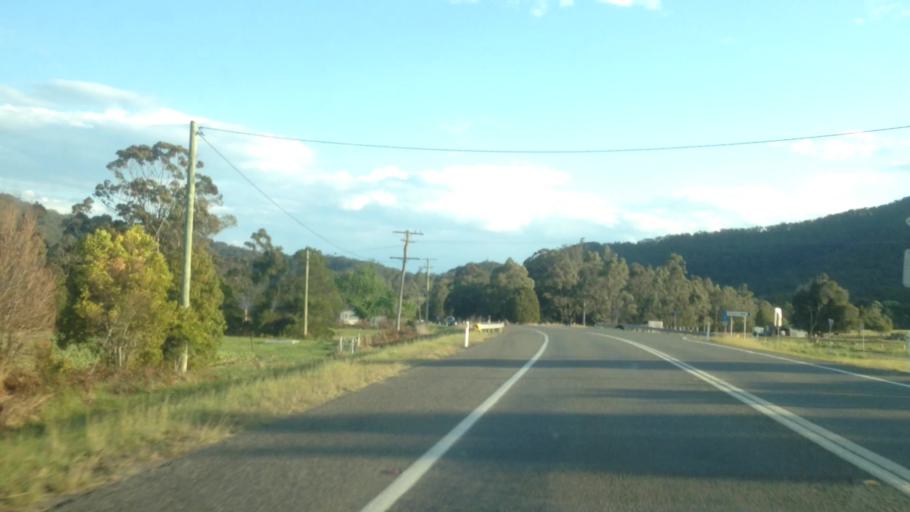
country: AU
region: New South Wales
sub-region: Lake Macquarie Shire
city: Holmesville
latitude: -32.9481
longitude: 151.4790
